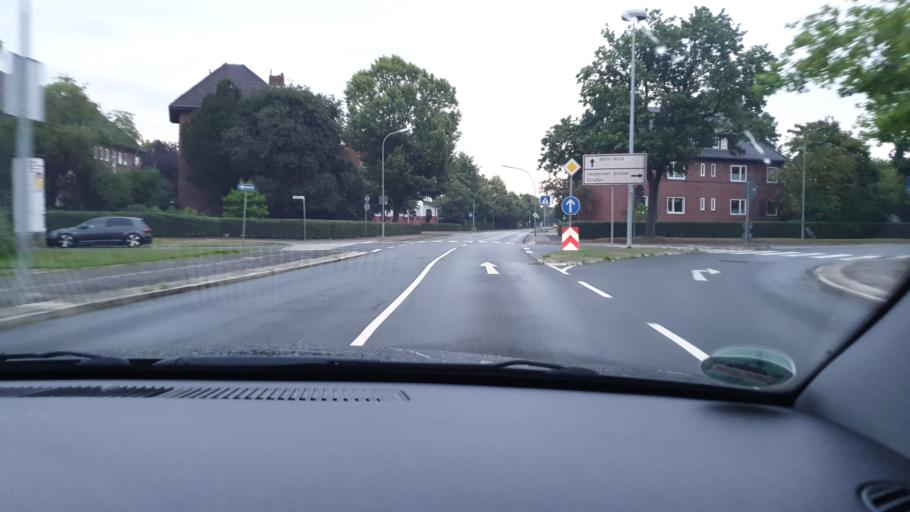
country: DE
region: Lower Saxony
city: Wilhelmshaven
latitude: 53.5286
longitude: 8.1133
